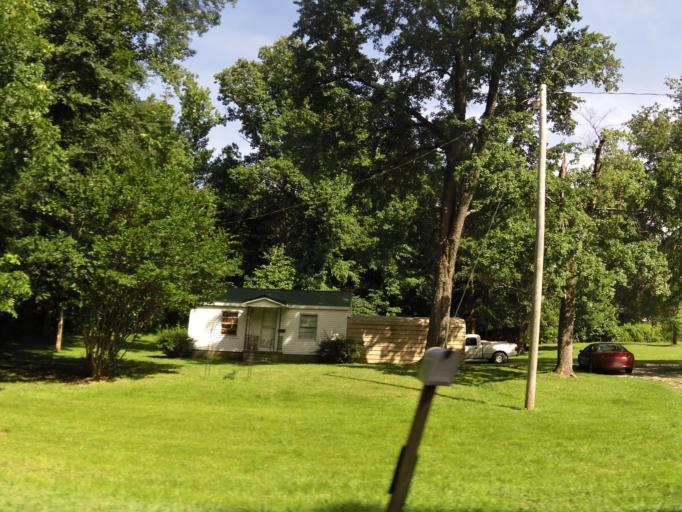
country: US
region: Tennessee
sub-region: Carroll County
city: Huntingdon
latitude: 36.0106
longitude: -88.4889
